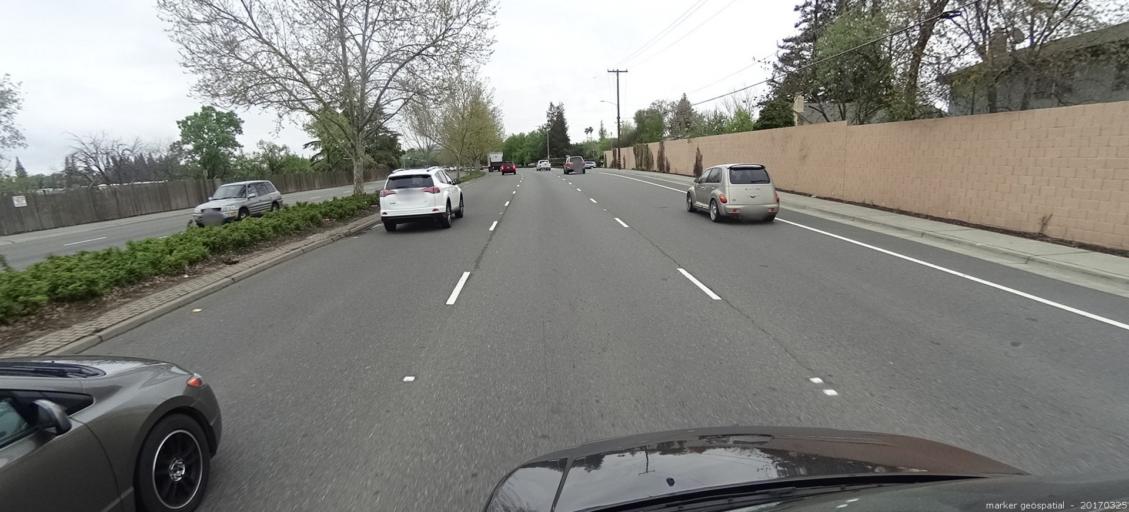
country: US
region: California
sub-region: Sacramento County
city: Rosemont
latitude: 38.5483
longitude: -121.3723
